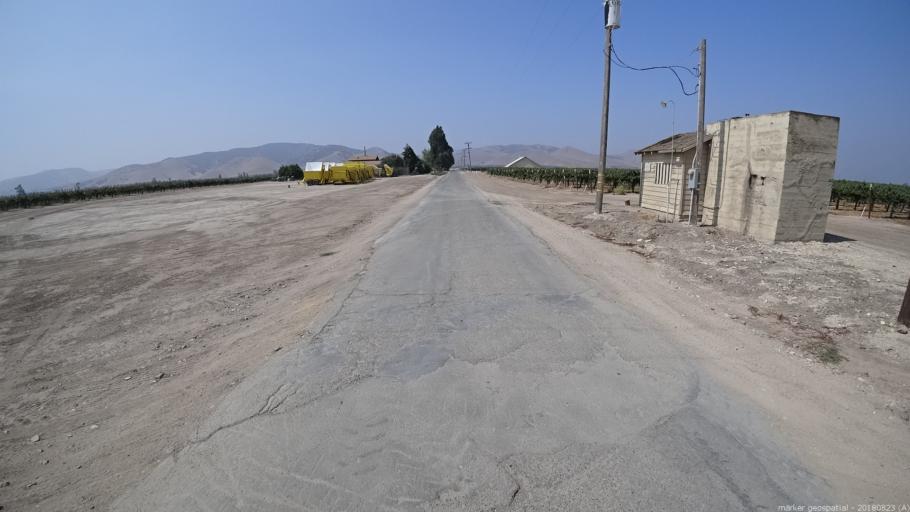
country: US
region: California
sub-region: Monterey County
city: Greenfield
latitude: 36.2683
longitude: -121.1993
